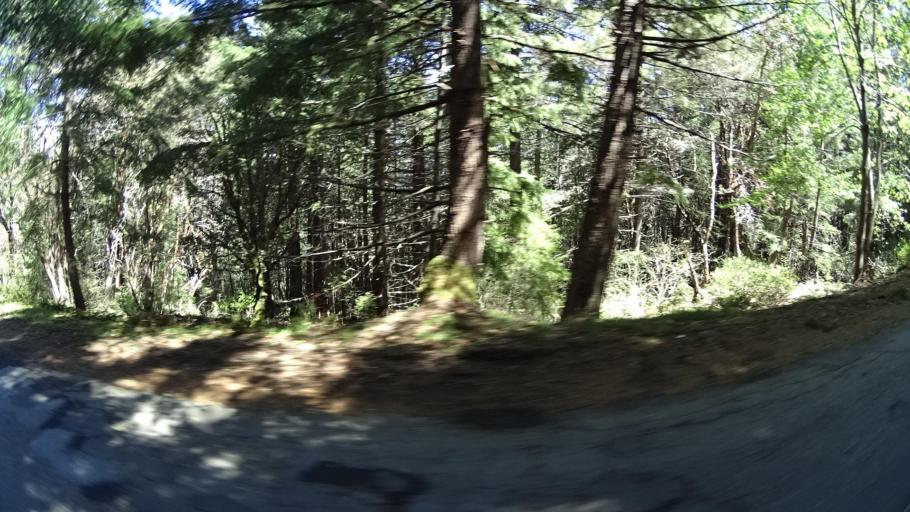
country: US
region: California
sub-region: Humboldt County
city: Rio Dell
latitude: 40.2904
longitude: -124.0562
